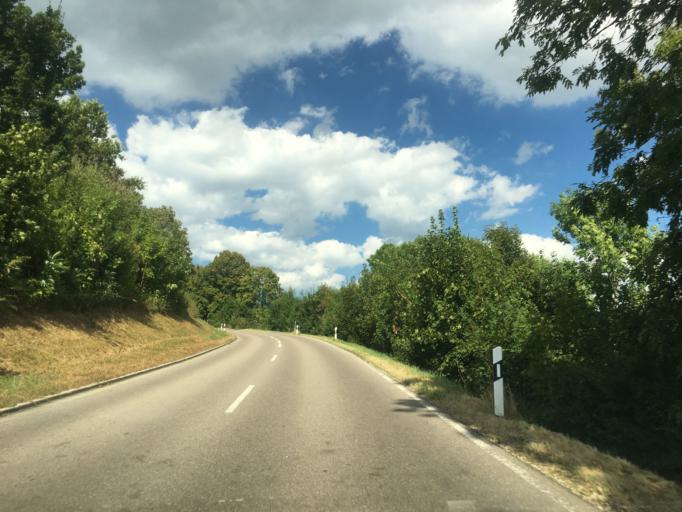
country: DE
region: Baden-Wuerttemberg
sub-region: Tuebingen Region
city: Hayingen
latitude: 48.2788
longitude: 9.4739
